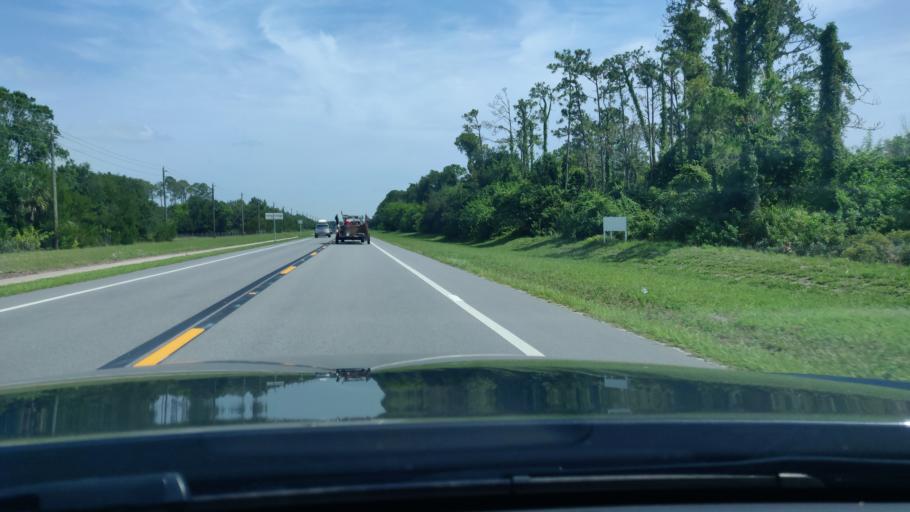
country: US
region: Florida
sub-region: Flagler County
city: Flagler Beach
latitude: 29.5088
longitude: -81.1614
